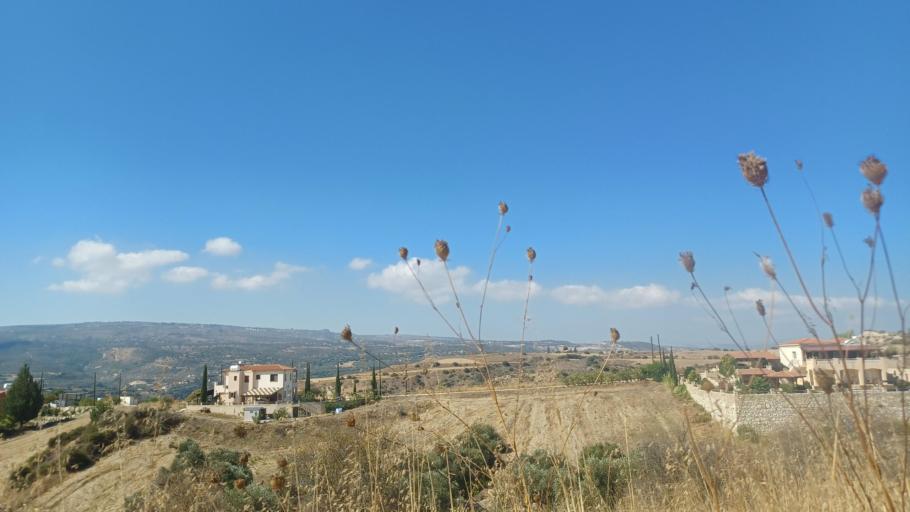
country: CY
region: Pafos
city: Polis
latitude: 34.9871
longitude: 32.4706
